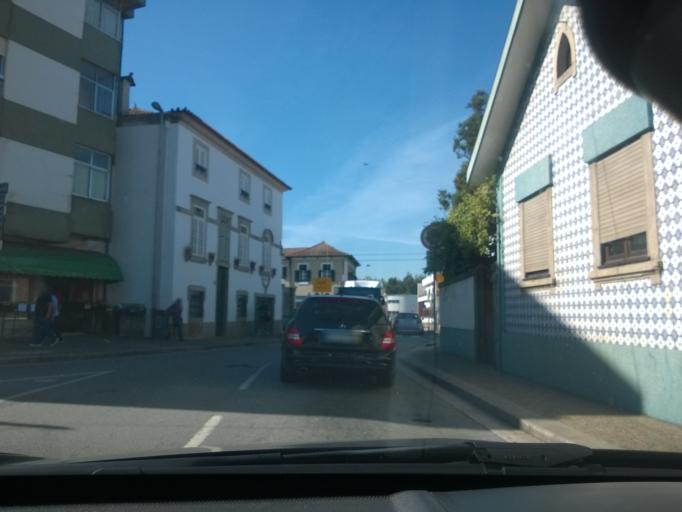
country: PT
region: Porto
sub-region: Maia
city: Gemunde
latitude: 41.2480
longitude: -8.6623
